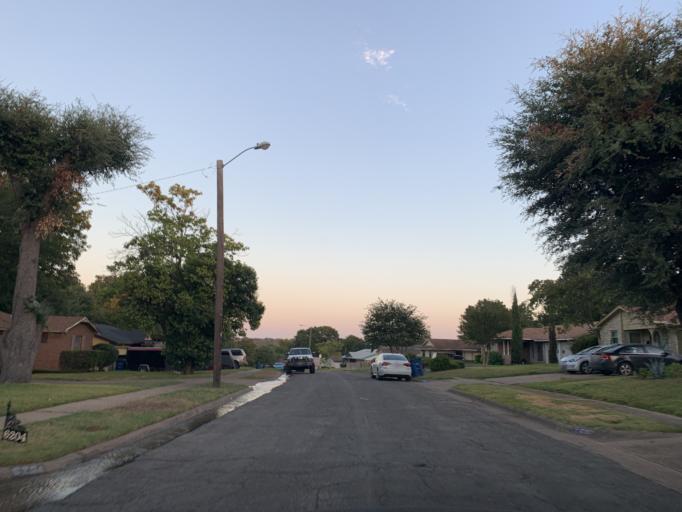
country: US
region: Texas
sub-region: Dallas County
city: Hutchins
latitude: 32.6728
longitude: -96.7996
